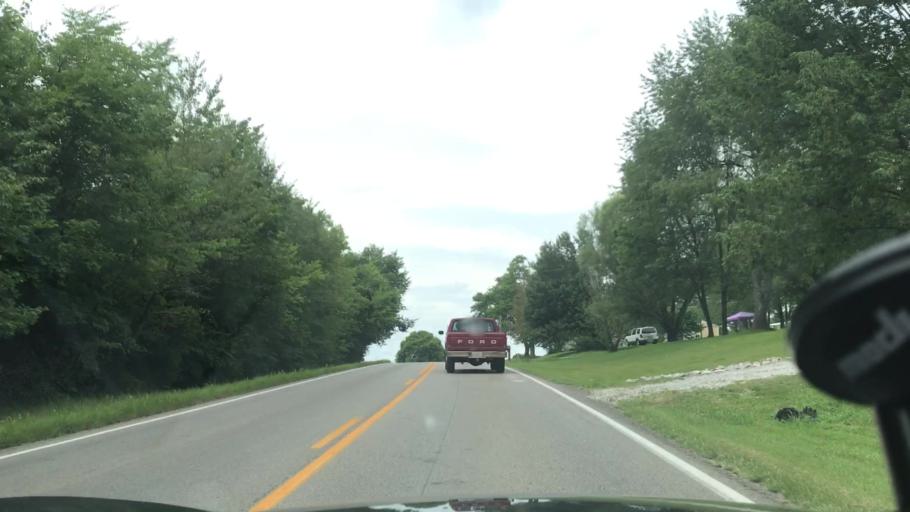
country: US
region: Kentucky
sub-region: Hart County
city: Horse Cave
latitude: 37.1757
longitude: -85.8678
